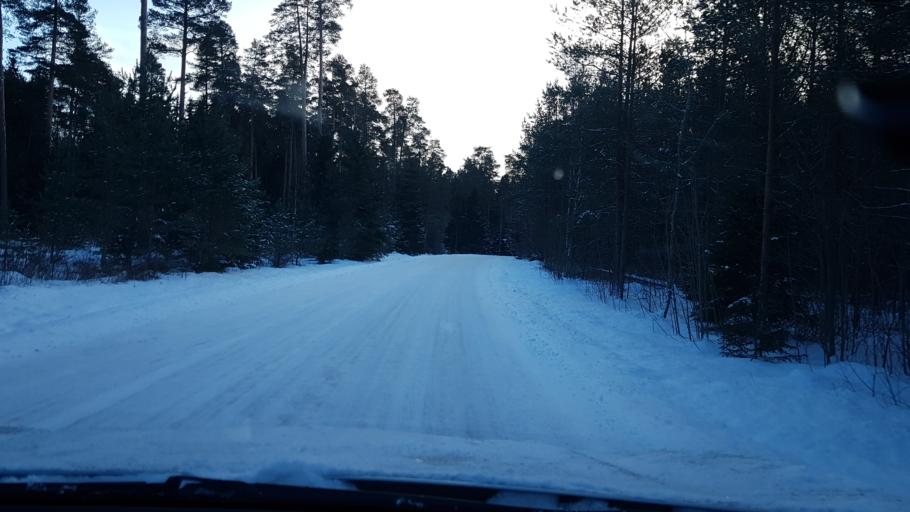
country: EE
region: Harju
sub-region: Nissi vald
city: Turba
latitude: 59.2116
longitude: 24.1414
